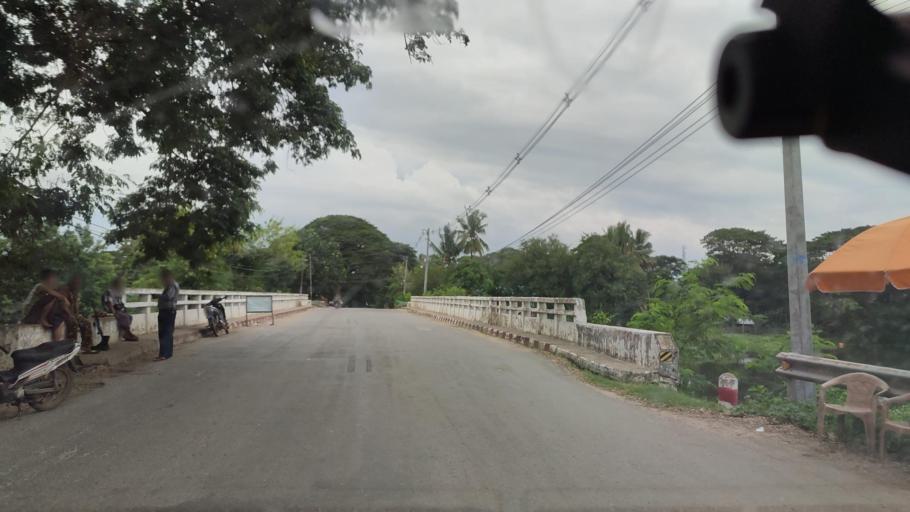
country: MM
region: Bago
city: Paungde
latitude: 18.5264
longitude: 95.3586
